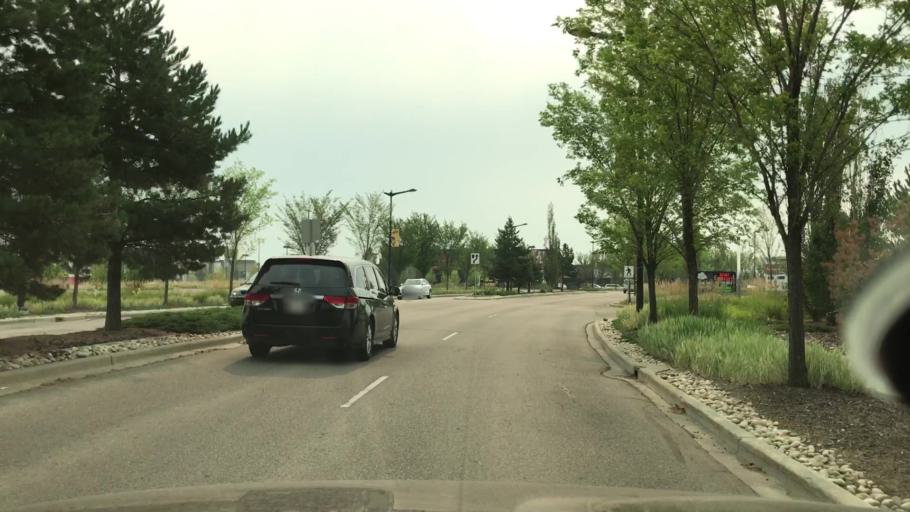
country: CA
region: Alberta
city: Devon
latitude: 53.4375
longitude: -113.6020
